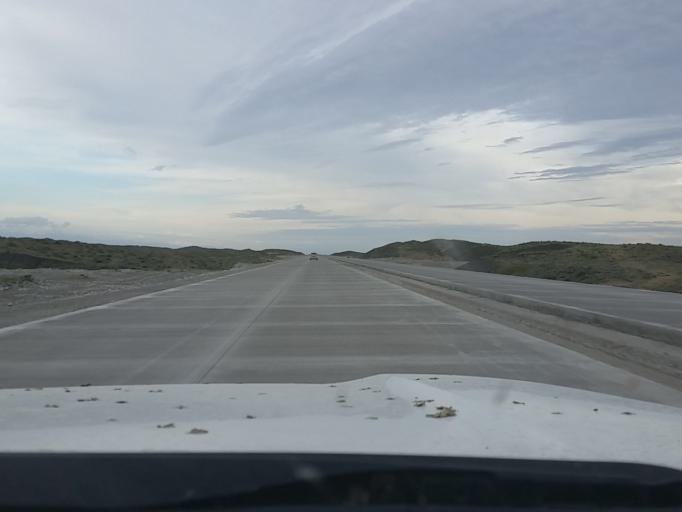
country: KZ
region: Almaty Oblysy
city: Zharkent
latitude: 44.1746
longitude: 80.3085
